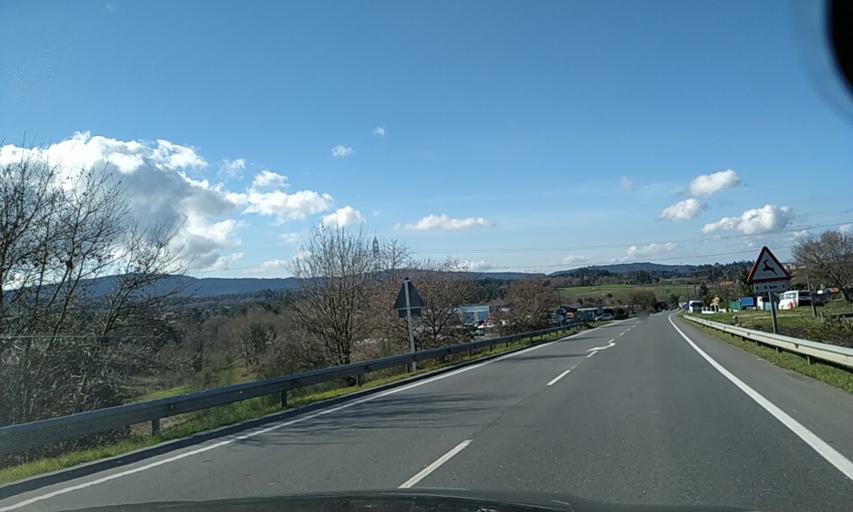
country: ES
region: Galicia
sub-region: Provincia de Pontevedra
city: Silleda
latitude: 42.7104
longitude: -8.2739
